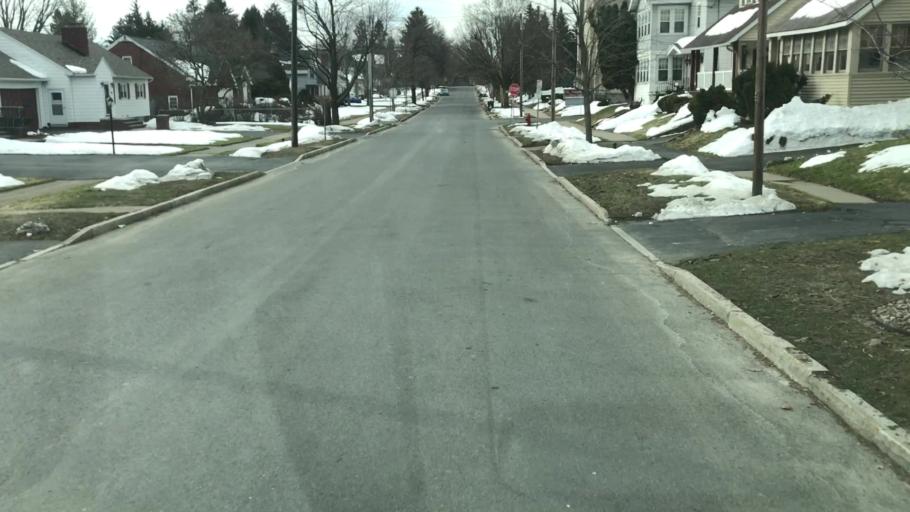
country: US
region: New York
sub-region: Onondaga County
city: Lyncourt
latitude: 43.0719
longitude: -76.1344
